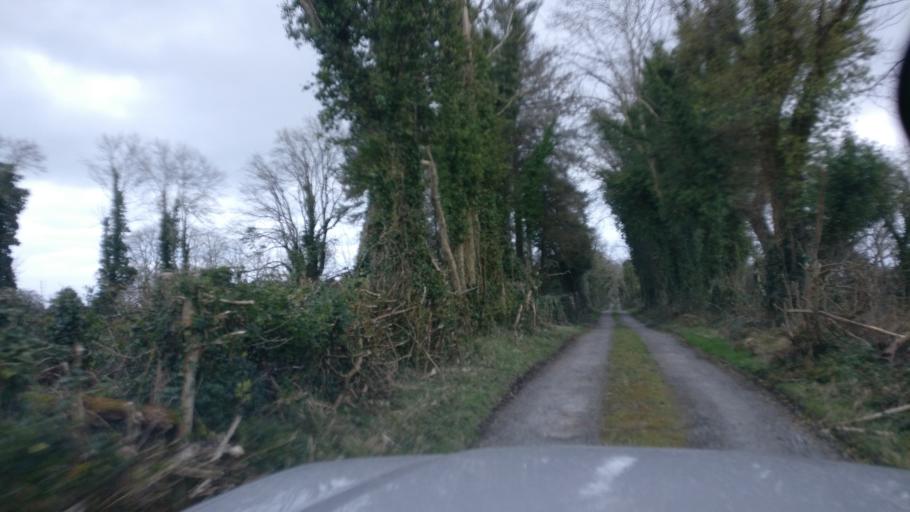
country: IE
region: Connaught
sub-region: County Galway
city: Loughrea
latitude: 53.2532
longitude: -8.4533
